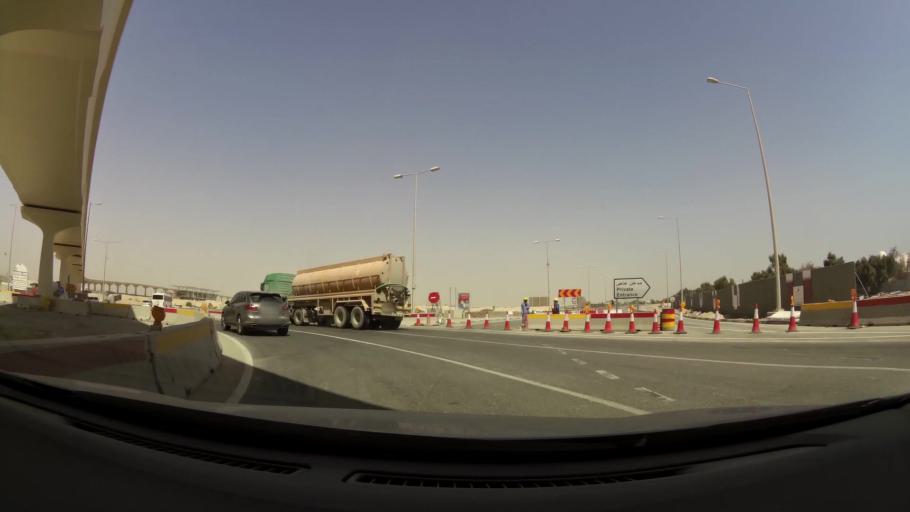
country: QA
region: Baladiyat ad Dawhah
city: Doha
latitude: 25.3780
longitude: 51.5004
